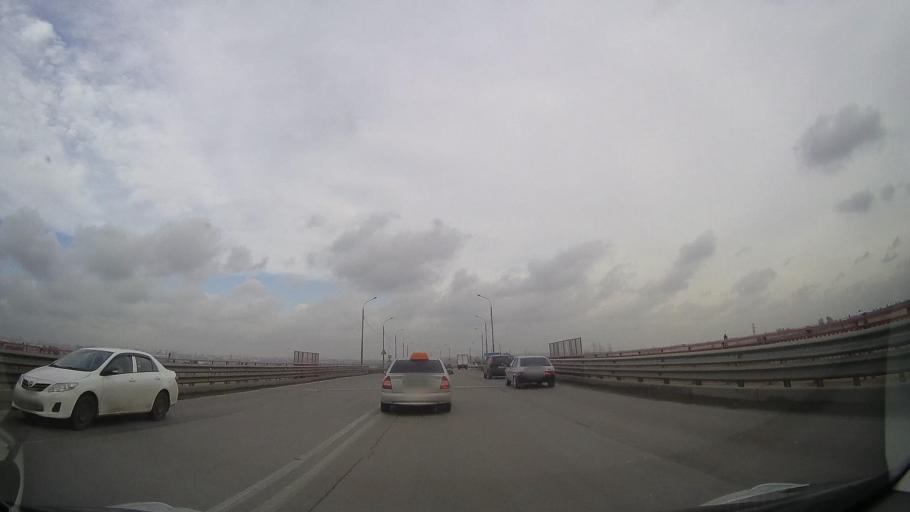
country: RU
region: Rostov
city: Bataysk
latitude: 47.1656
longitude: 39.7431
